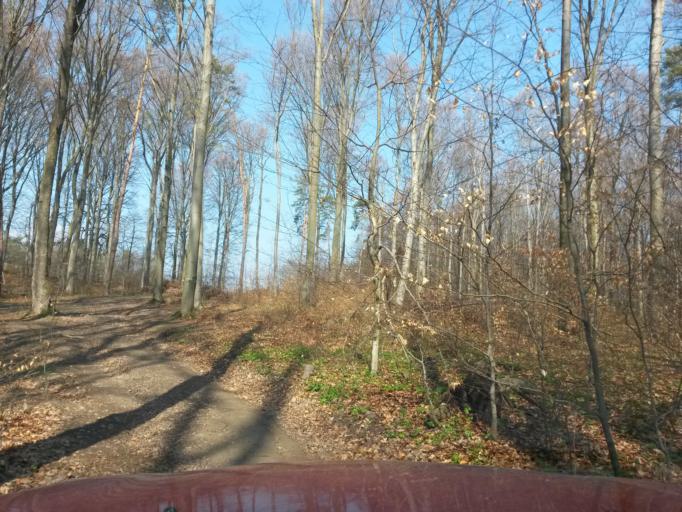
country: SK
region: Presovsky
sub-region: Okres Presov
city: Presov
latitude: 48.9288
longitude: 21.1545
